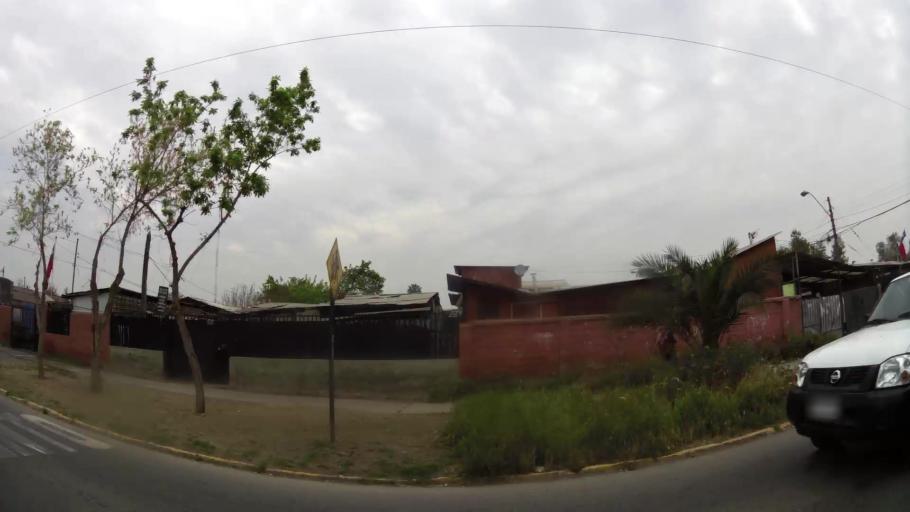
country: CL
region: Santiago Metropolitan
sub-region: Provincia de Santiago
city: Villa Presidente Frei, Nunoa, Santiago, Chile
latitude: -33.5047
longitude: -70.5990
